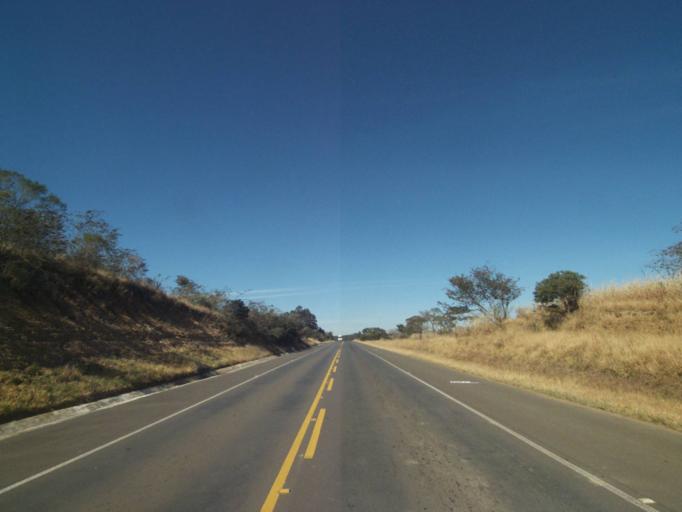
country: BR
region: Parana
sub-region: Tibagi
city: Tibagi
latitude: -24.7651
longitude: -50.4692
